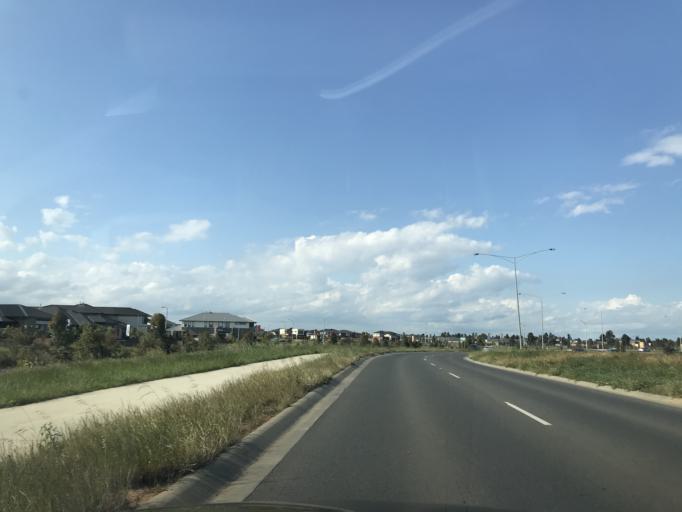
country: AU
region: Victoria
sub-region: Wyndham
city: Hoppers Crossing
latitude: -37.8968
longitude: 144.7131
